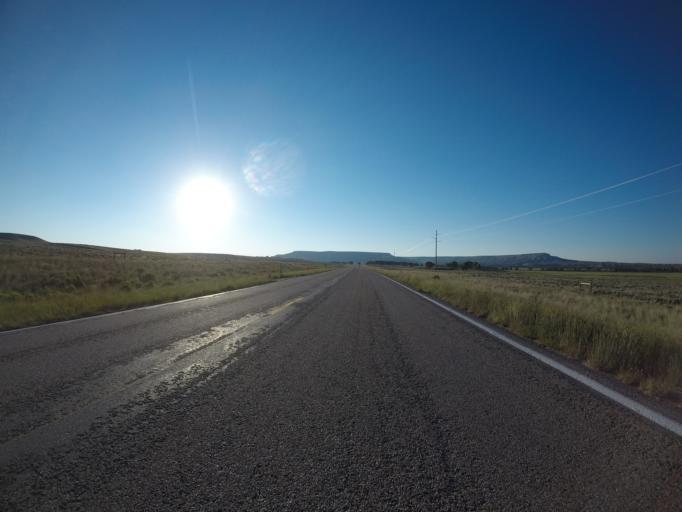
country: US
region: Wyoming
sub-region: Sublette County
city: Marbleton
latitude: 42.5718
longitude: -109.9724
